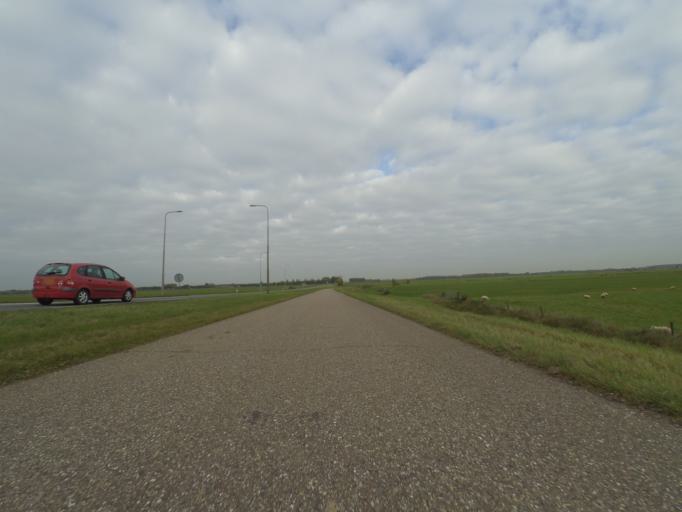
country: NL
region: Gelderland
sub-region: Gemeente Nijkerk
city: Nijkerk
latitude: 52.2465
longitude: 5.4791
